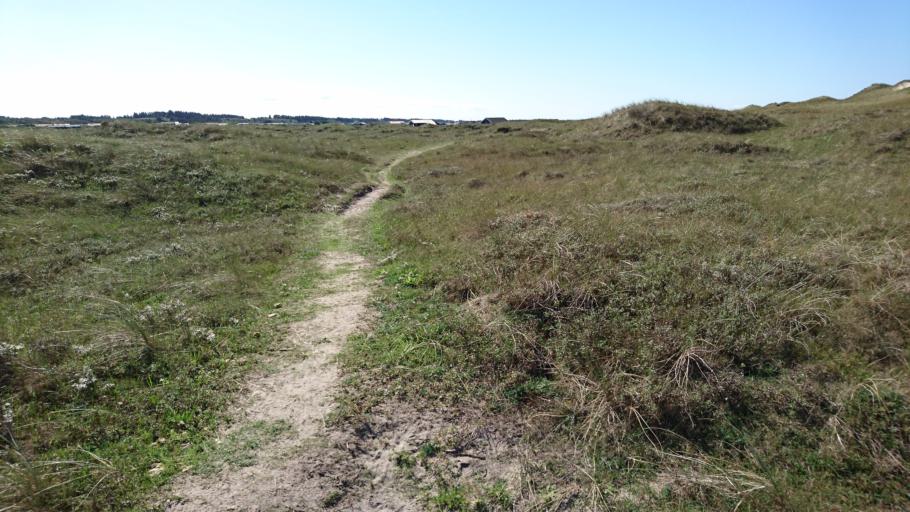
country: DK
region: North Denmark
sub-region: Hjorring Kommune
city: Hirtshals
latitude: 57.5170
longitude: 9.8693
